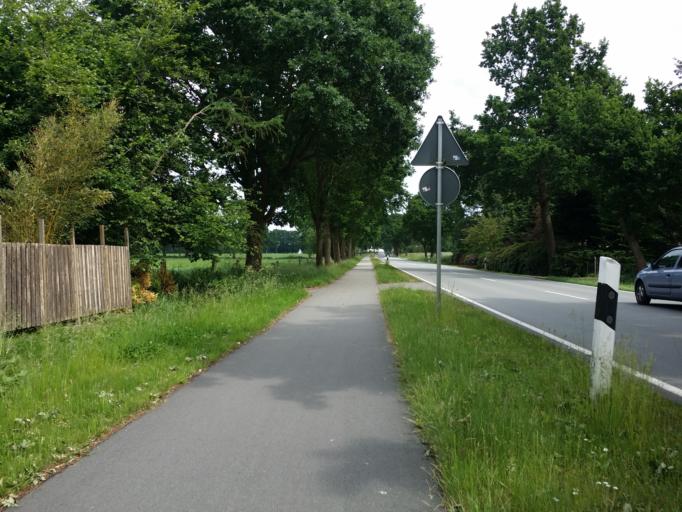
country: DE
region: Lower Saxony
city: Wiefelstede
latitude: 53.2445
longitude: 8.1446
